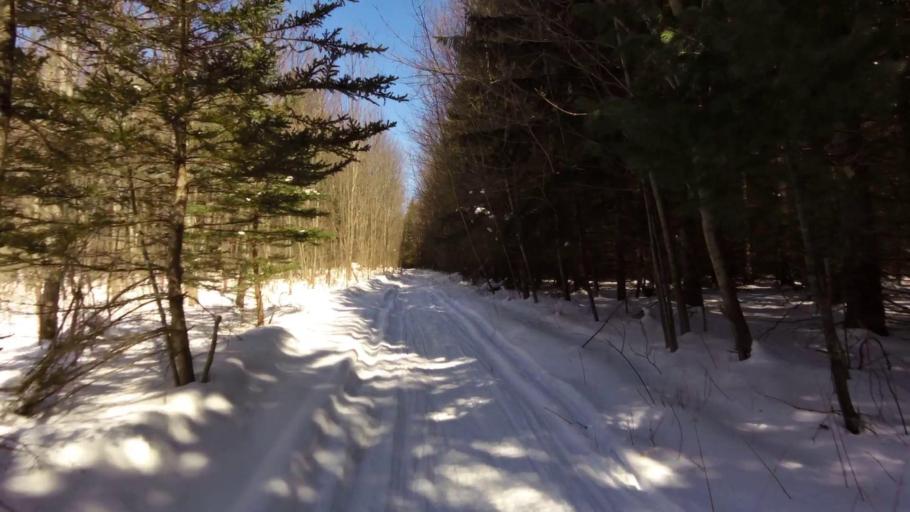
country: US
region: New York
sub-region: Allegany County
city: Houghton
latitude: 42.3603
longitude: -78.1794
